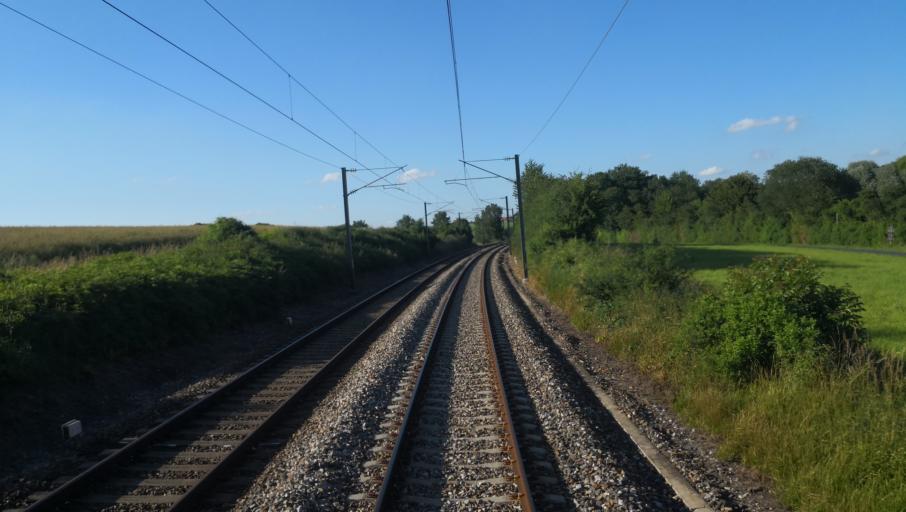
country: FR
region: Ile-de-France
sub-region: Departement des Yvelines
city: Breval
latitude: 48.9236
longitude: 1.5191
